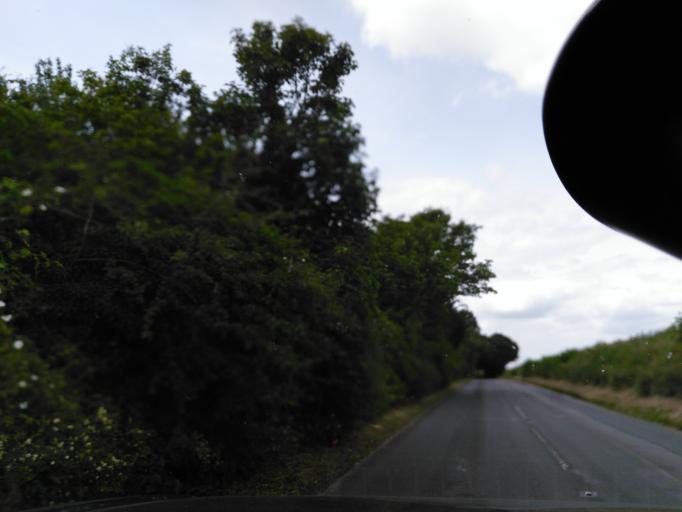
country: GB
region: England
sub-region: Wiltshire
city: Woodford
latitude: 51.0920
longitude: -1.8286
